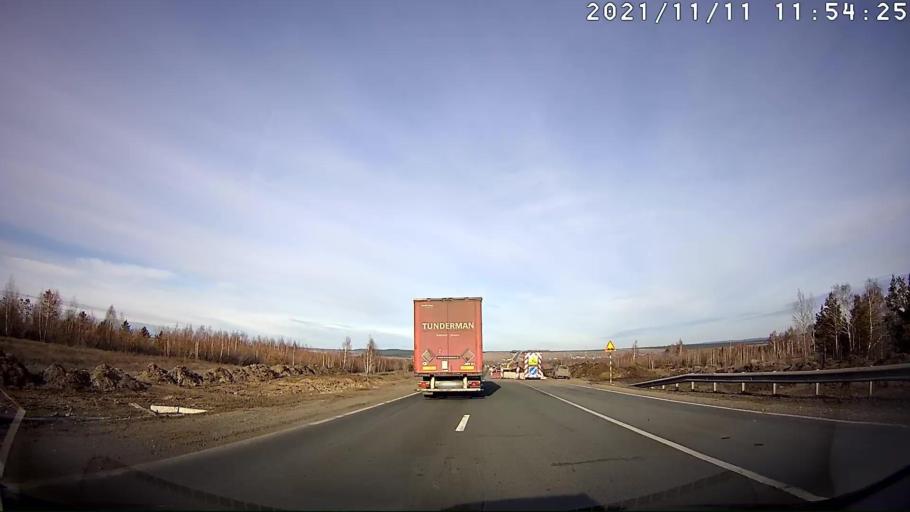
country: RU
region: Samara
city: Varlamovo
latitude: 53.5311
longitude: 48.3398
